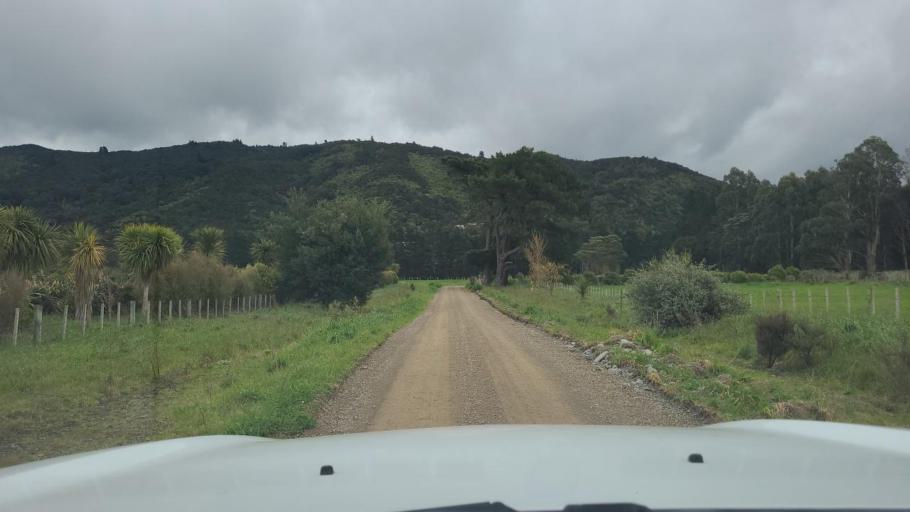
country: NZ
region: Wellington
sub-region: Upper Hutt City
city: Upper Hutt
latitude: -41.1203
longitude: 175.3136
